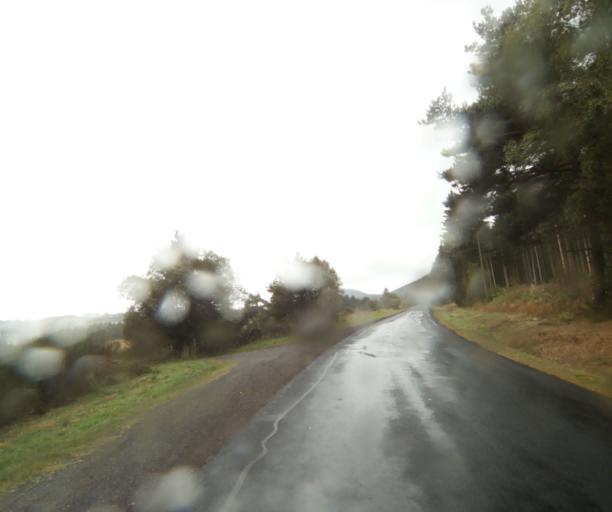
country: FR
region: Auvergne
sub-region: Departement du Puy-de-Dome
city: Orcines
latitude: 45.7556
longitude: 2.9777
